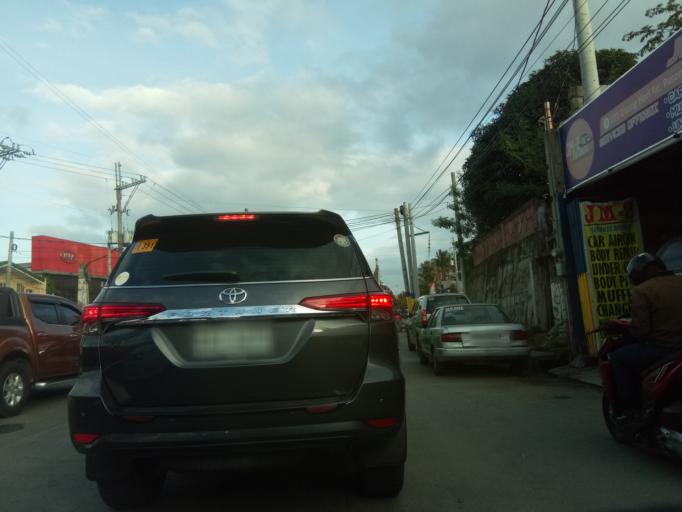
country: PH
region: Calabarzon
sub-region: Province of Cavite
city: Imus
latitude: 14.3868
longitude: 120.9744
